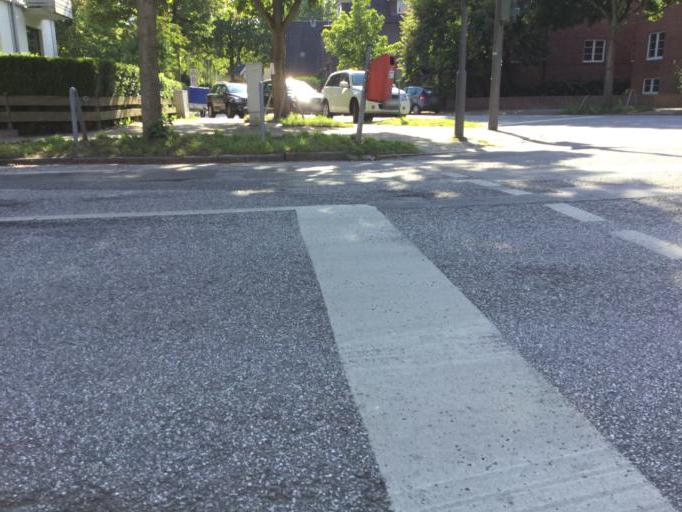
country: DE
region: Hamburg
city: Fuhlsbuettel
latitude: 53.6351
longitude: 10.0253
